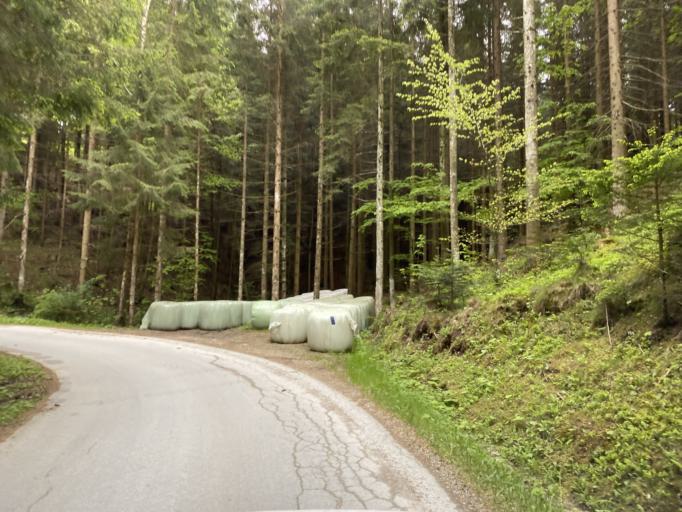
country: AT
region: Styria
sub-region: Politischer Bezirk Weiz
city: Gschaid bei Birkfeld
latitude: 47.3362
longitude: 15.7273
